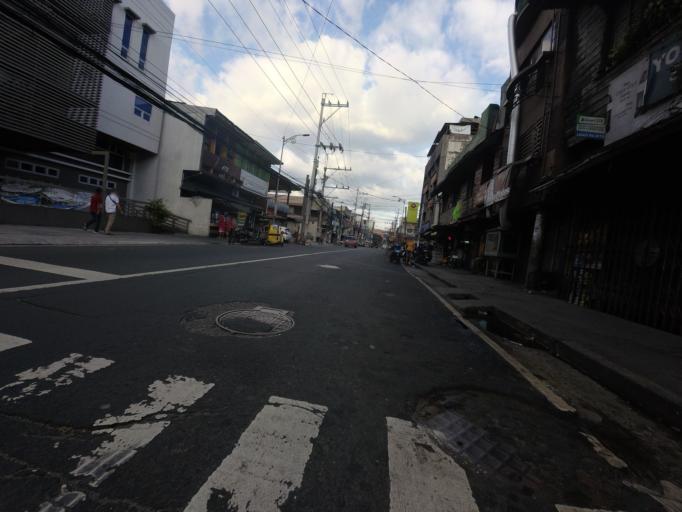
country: PH
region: Metro Manila
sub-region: City of Manila
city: Quiapo
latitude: 14.5773
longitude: 120.9912
